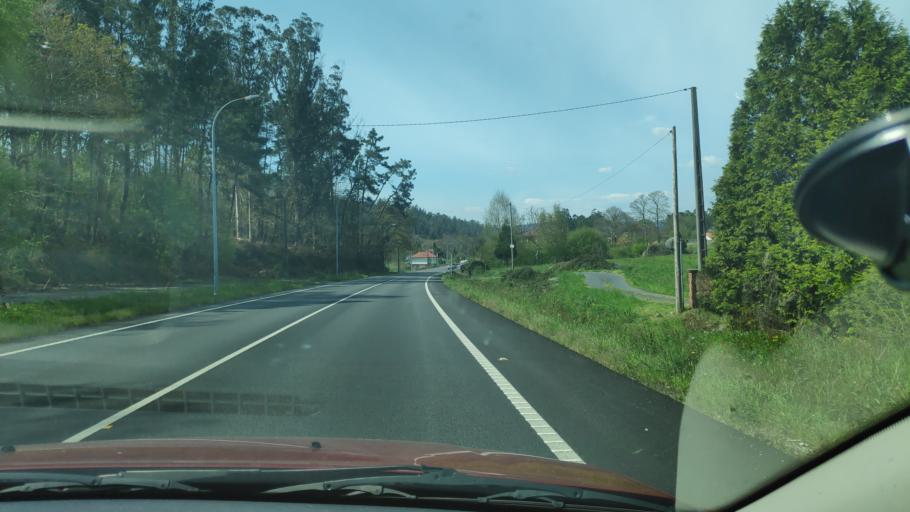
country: ES
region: Galicia
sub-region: Provincia da Coruna
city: Ames
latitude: 42.8820
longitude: -8.6806
